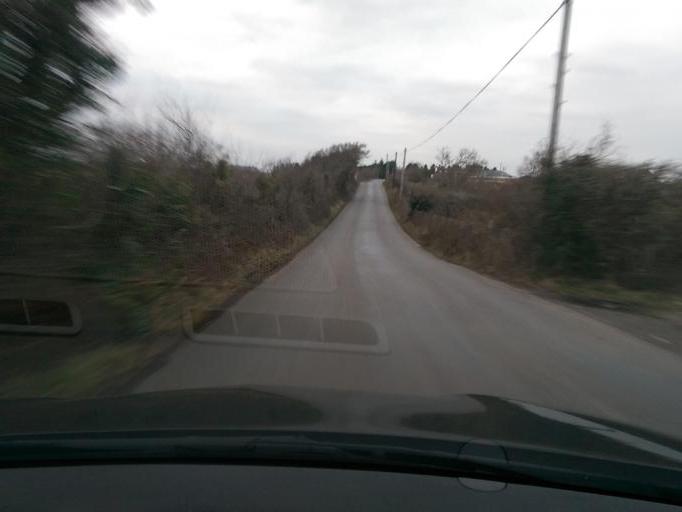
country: IE
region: Connaught
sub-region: County Galway
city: Bearna
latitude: 53.2742
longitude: -9.1611
